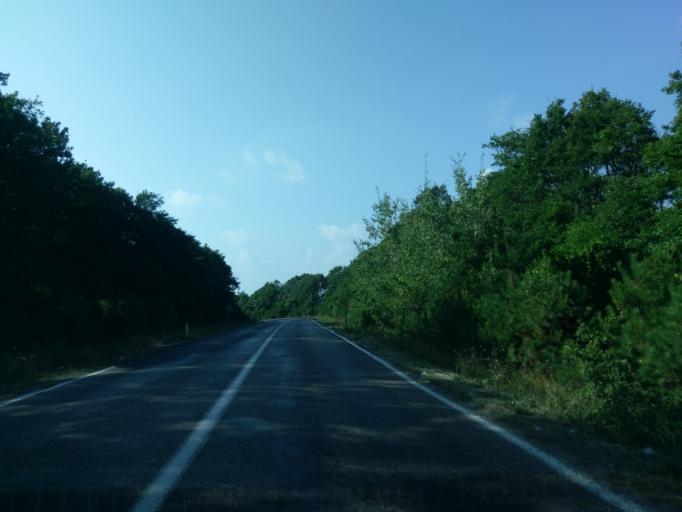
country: TR
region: Sinop
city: Yenikonak
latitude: 41.9416
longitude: 34.7093
